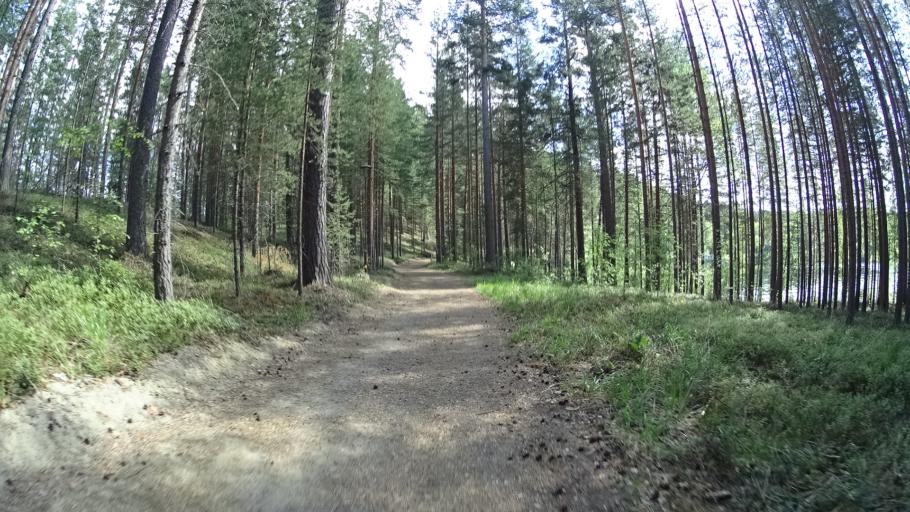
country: FI
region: Southern Savonia
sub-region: Savonlinna
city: Punkaharju
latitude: 61.7913
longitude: 29.3054
